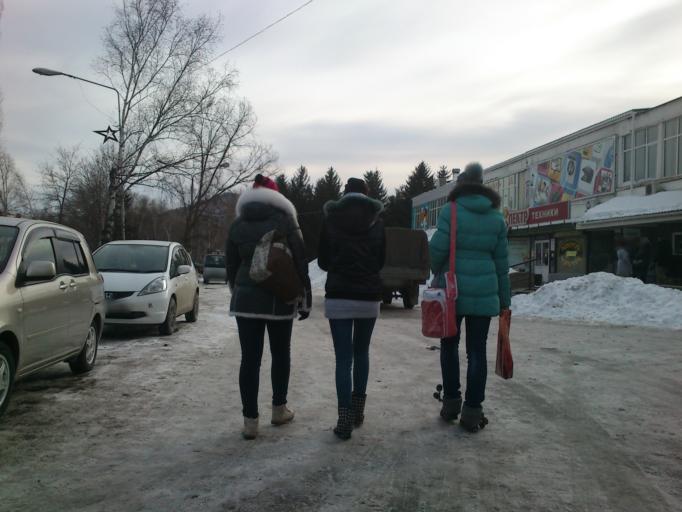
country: RU
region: Primorskiy
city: Kavalerovo
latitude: 44.2621
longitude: 135.0579
